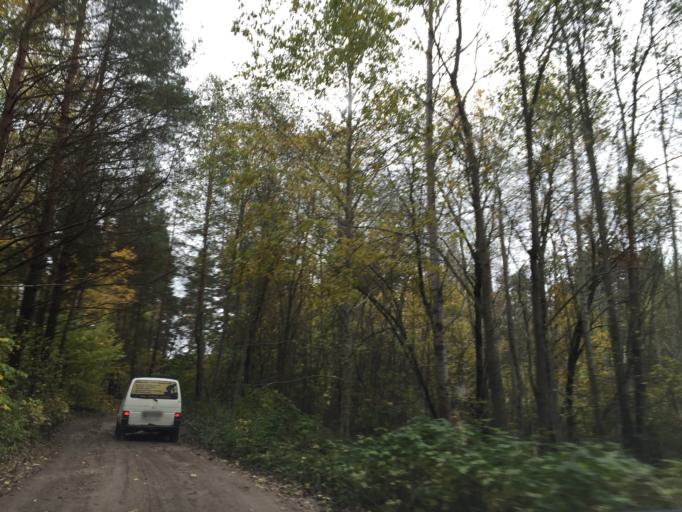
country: LV
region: Ogre
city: Ogre
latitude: 56.7974
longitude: 24.6476
